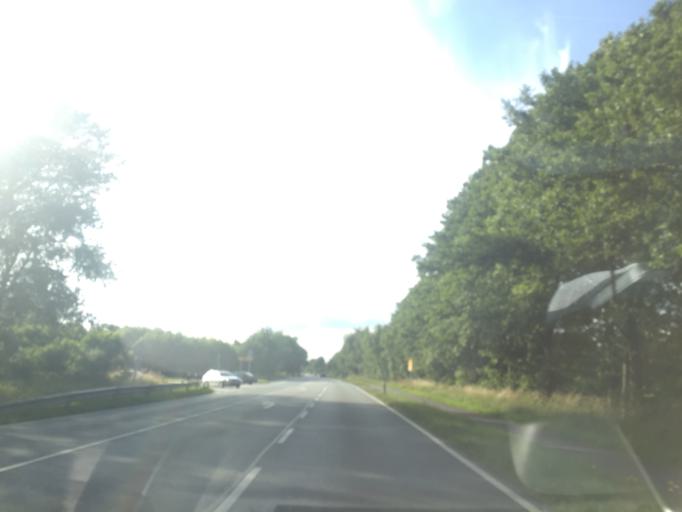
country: DE
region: Schleswig-Holstein
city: Harrislee
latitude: 54.7789
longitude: 9.3808
